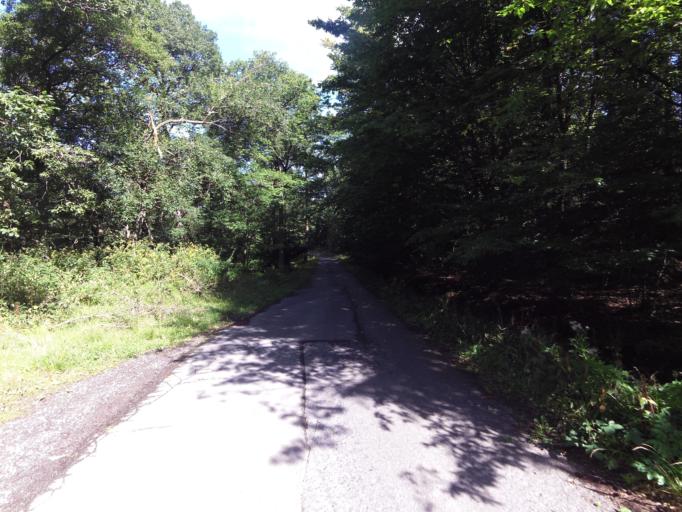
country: BE
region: Wallonia
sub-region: Province du Luxembourg
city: Nassogne
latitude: 50.1225
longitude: 5.3710
